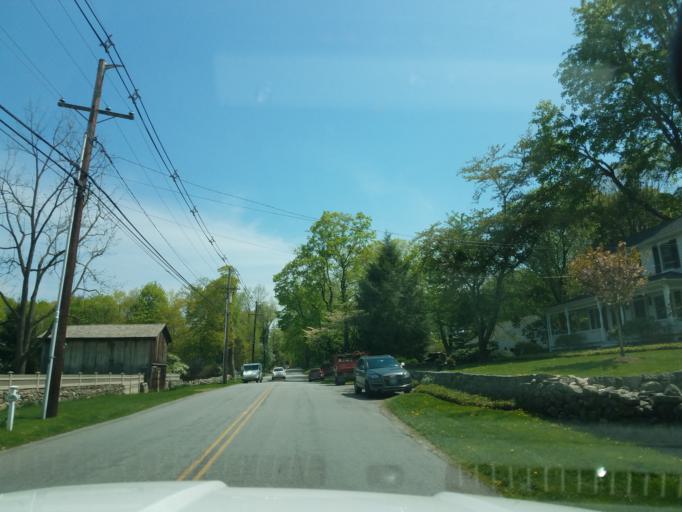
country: US
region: Connecticut
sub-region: Fairfield County
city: New Canaan
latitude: 41.1297
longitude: -73.4763
